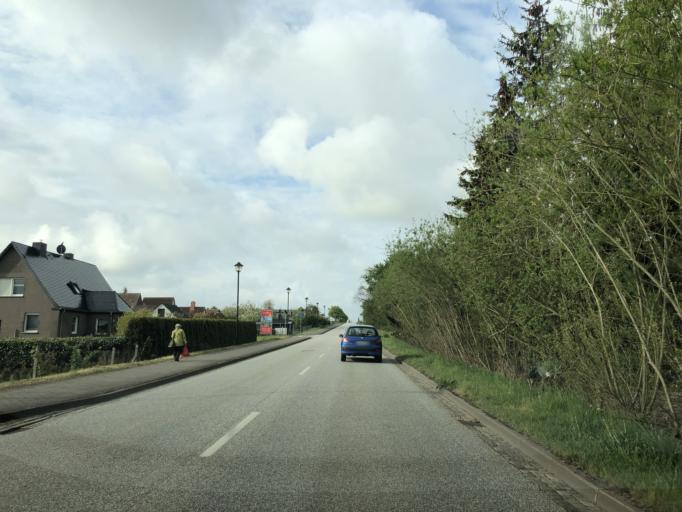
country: DE
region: Mecklenburg-Vorpommern
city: Goldberg
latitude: 53.5812
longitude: 12.0840
